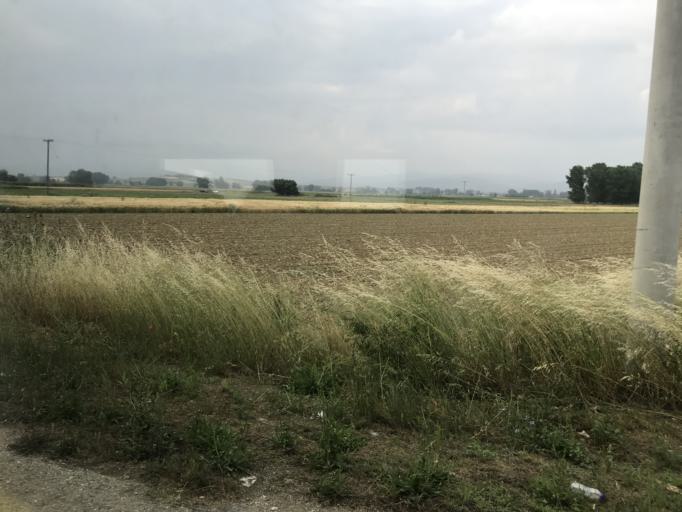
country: GR
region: East Macedonia and Thrace
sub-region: Nomos Rodopis
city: Arisvi
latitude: 41.0557
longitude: 25.6127
